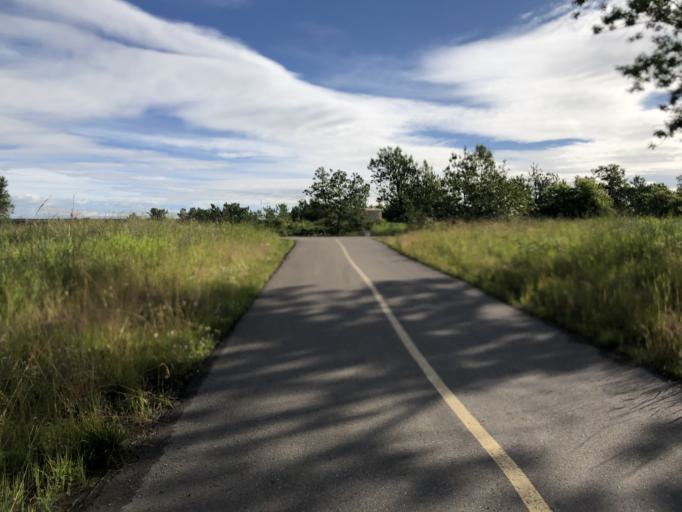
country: CA
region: Alberta
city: Calgary
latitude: 51.0060
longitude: -114.0186
